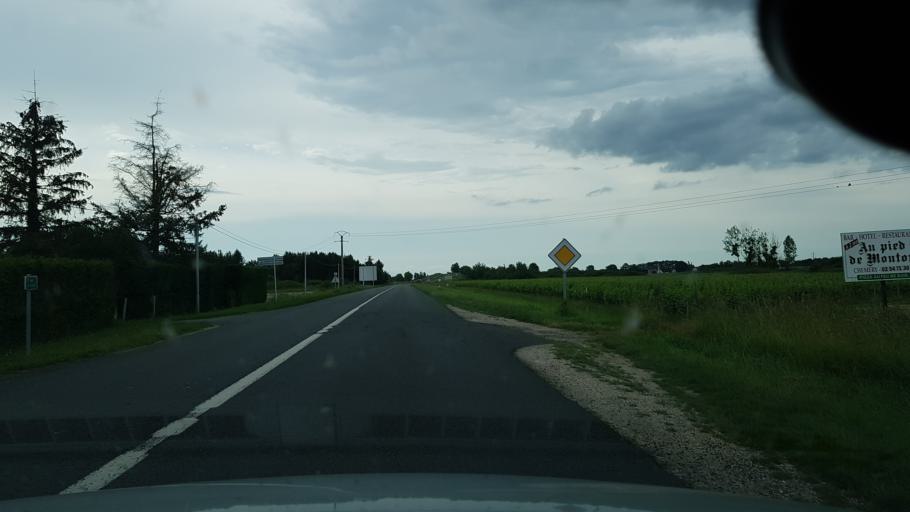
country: FR
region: Centre
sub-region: Departement du Loir-et-Cher
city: Chatillon-sur-Cher
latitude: 47.3216
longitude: 1.4958
